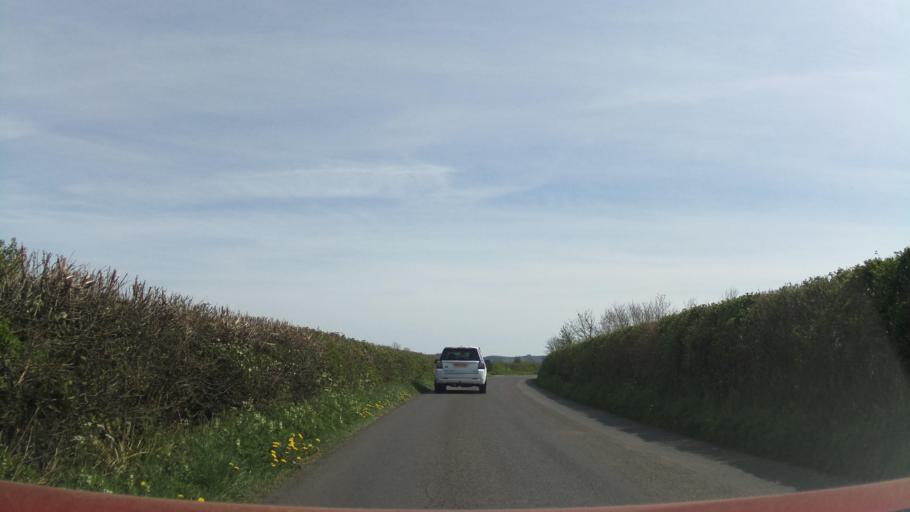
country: GB
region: England
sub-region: Somerset
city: Yeovil
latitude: 51.0166
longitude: -2.5948
